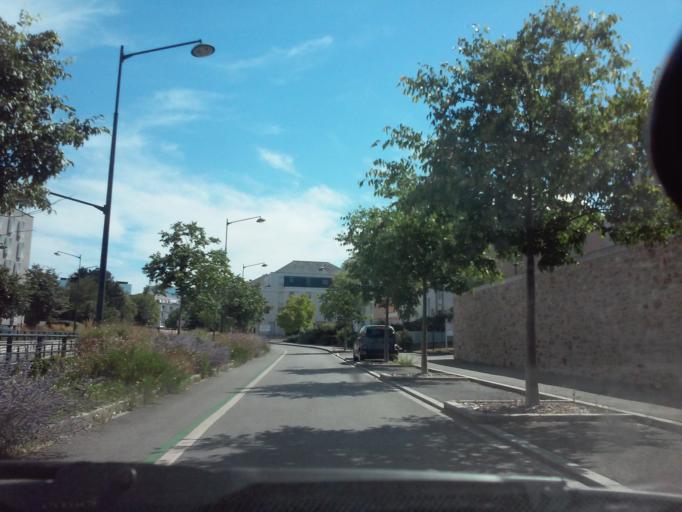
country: FR
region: Brittany
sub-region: Departement d'Ille-et-Vilaine
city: Rennes
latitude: 48.1014
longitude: -1.6948
